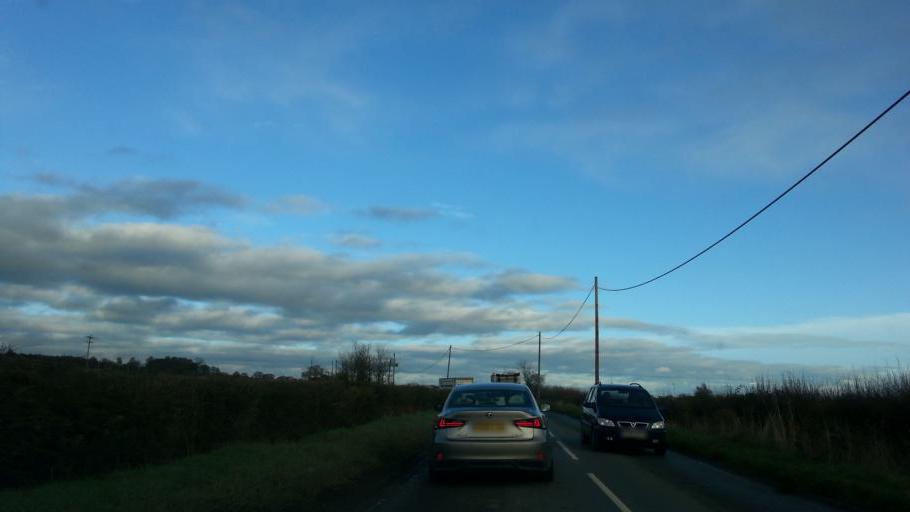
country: GB
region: England
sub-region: Oxfordshire
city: Faringdon
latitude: 51.6189
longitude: -1.5932
